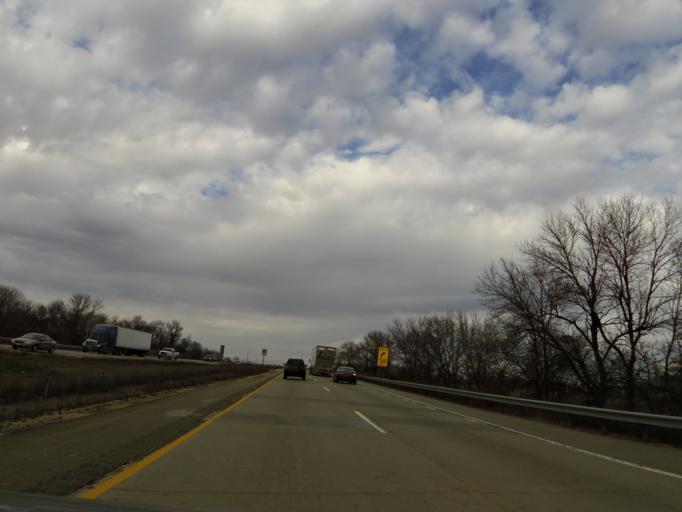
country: US
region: Wisconsin
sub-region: Rock County
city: Edgerton
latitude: 42.8309
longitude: -89.0266
